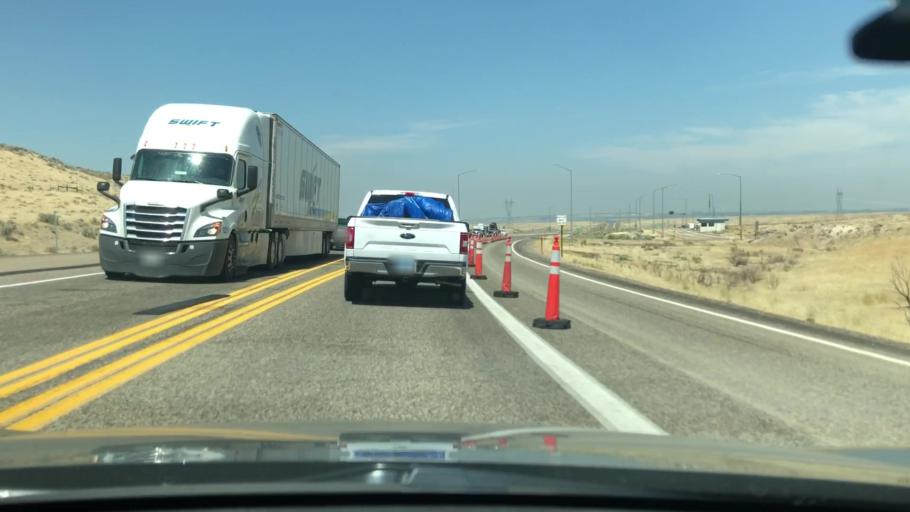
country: US
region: Idaho
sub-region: Owyhee County
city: Marsing
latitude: 43.4616
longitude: -116.8665
